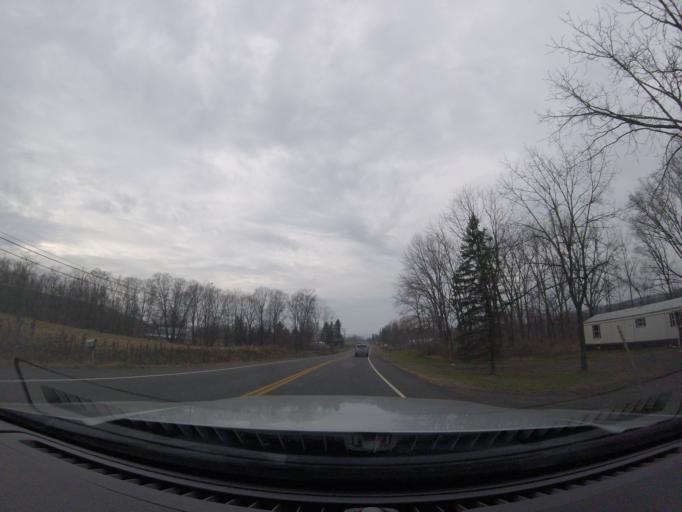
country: US
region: New York
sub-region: Schuyler County
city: Watkins Glen
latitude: 42.4242
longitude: -76.8159
